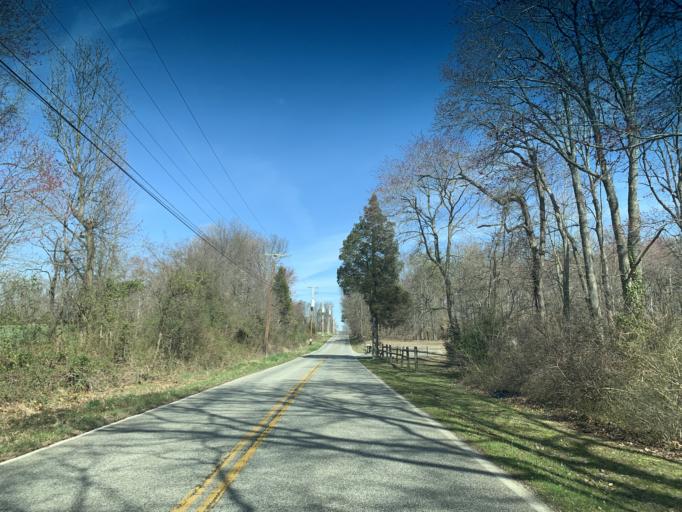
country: US
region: Maryland
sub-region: Cecil County
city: Charlestown
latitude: 39.5521
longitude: -76.0109
